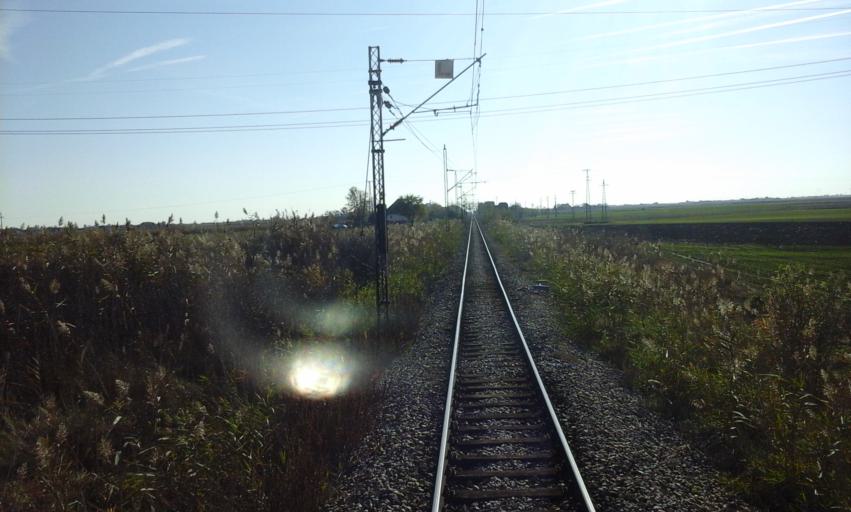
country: RS
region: Autonomna Pokrajina Vojvodina
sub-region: Severnobacki Okrug
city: Subotica
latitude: 46.0329
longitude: 19.6826
